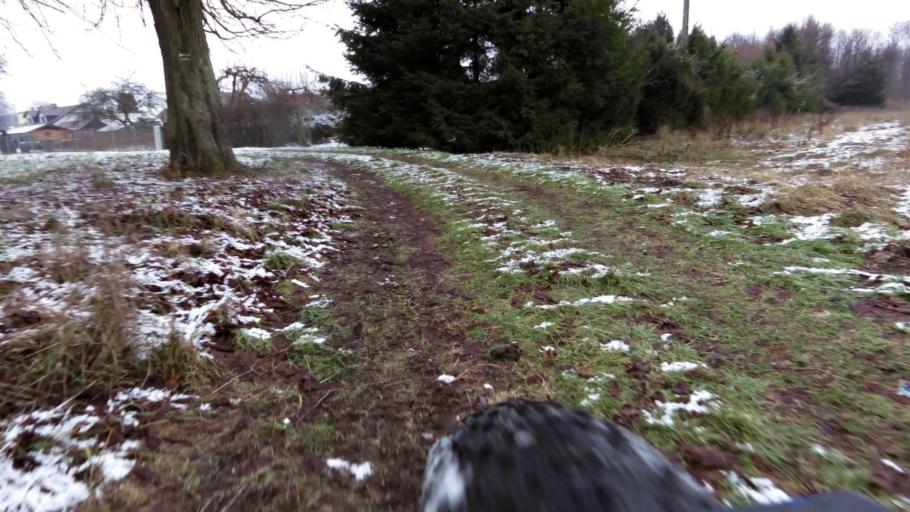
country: PL
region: West Pomeranian Voivodeship
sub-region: Powiat walecki
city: Miroslawiec
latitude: 53.3402
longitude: 16.0970
